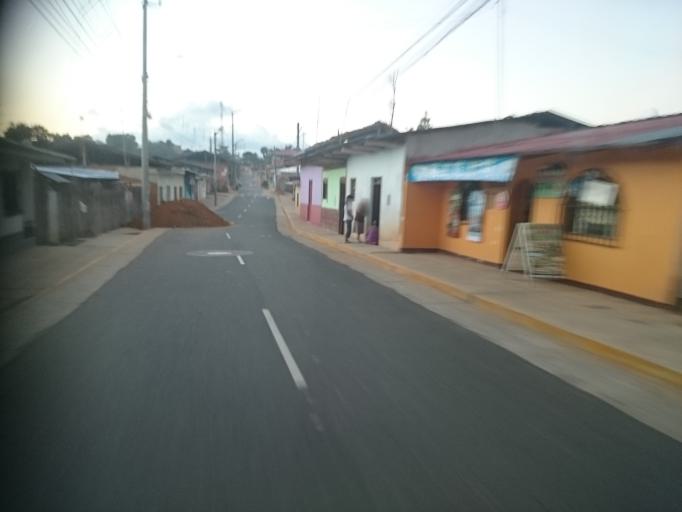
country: PE
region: San Martin
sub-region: Provincia de Lamas
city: Lamas
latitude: -6.4269
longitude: -76.5138
